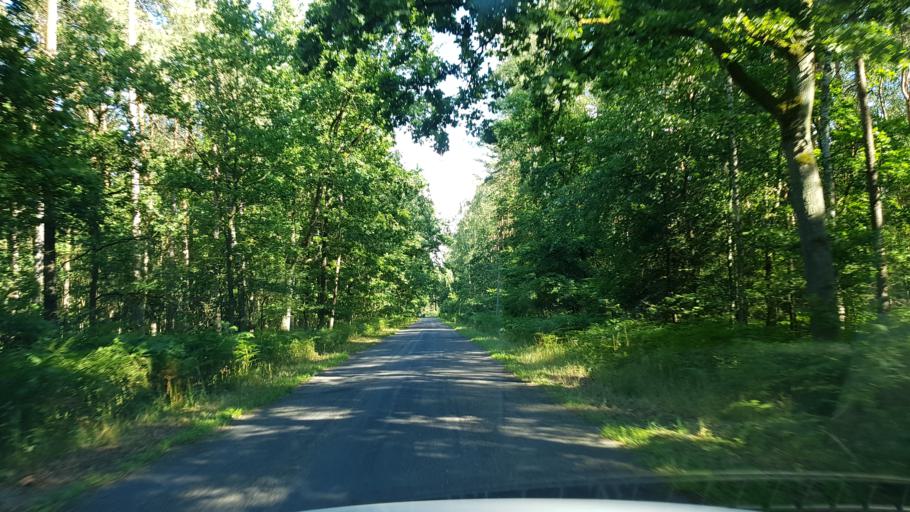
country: PL
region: West Pomeranian Voivodeship
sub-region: Powiat goleniowski
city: Goleniow
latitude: 53.5530
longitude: 14.7721
